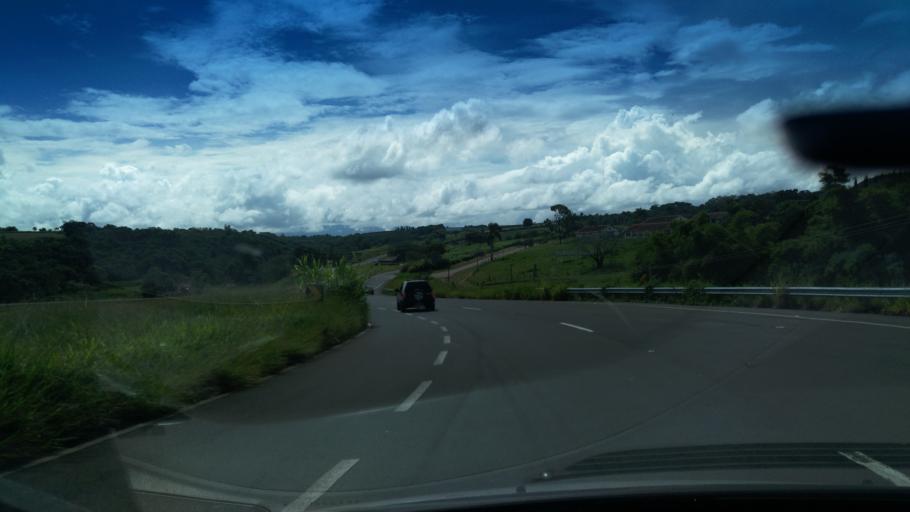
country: BR
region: Sao Paulo
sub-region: Santo Antonio Do Jardim
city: Espirito Santo do Pinhal
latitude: -22.1678
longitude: -46.7397
